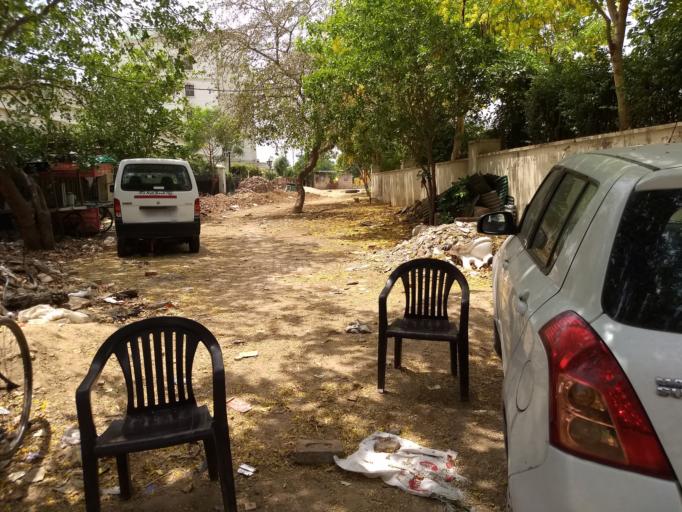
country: IN
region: Haryana
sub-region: Gurgaon
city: Gurgaon
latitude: 28.4937
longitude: 77.1053
